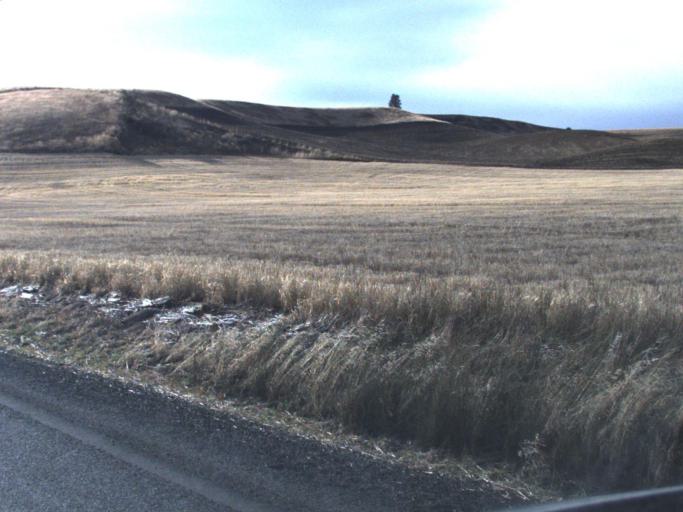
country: US
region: Washington
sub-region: Whitman County
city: Colfax
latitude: 46.8777
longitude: -117.3965
